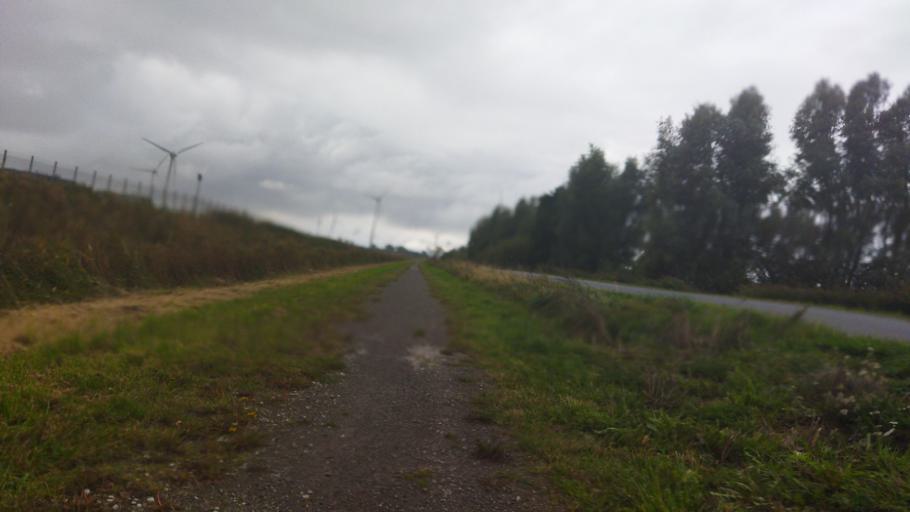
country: DE
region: Lower Saxony
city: Emden
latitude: 53.3517
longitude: 7.1442
